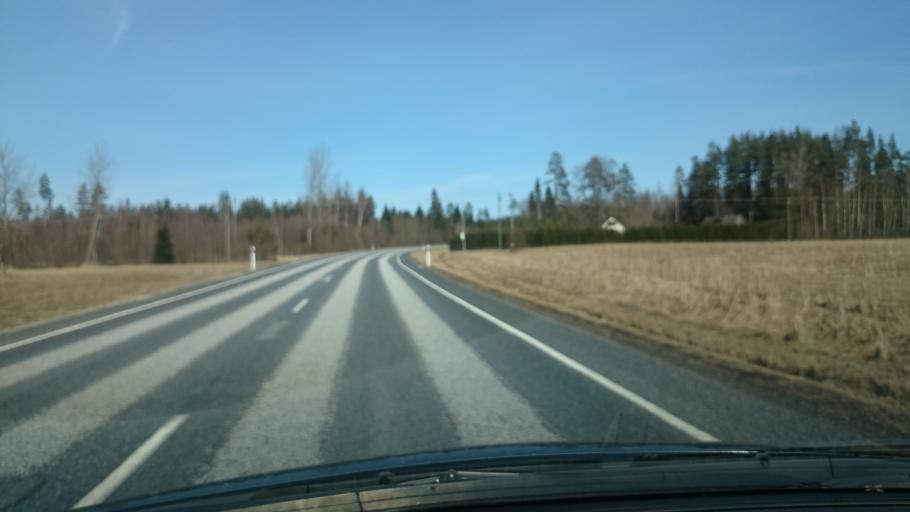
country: EE
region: Jaervamaa
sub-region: Tueri vald
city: Sarevere
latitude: 58.7303
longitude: 25.2872
